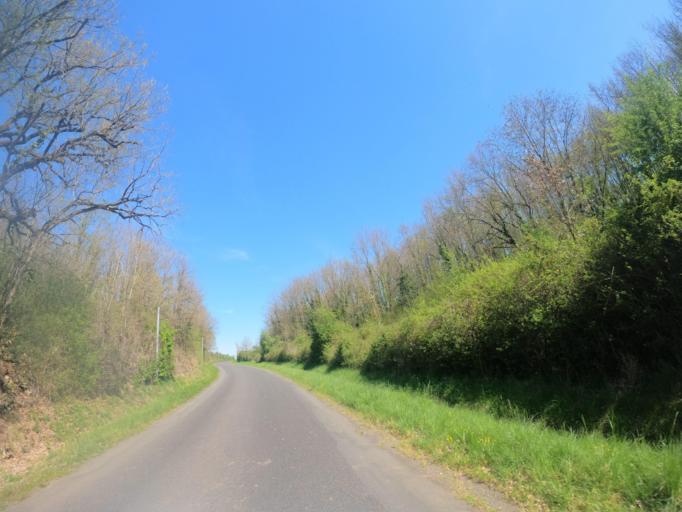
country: FR
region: Poitou-Charentes
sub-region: Departement des Deux-Sevres
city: Airvault
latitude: 46.8756
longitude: -0.1395
